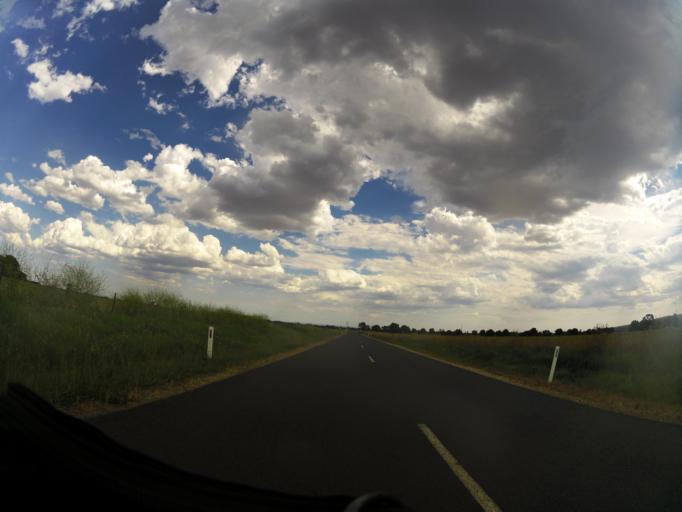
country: AU
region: Victoria
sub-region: Wellington
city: Heyfield
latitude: -37.9884
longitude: 146.6933
